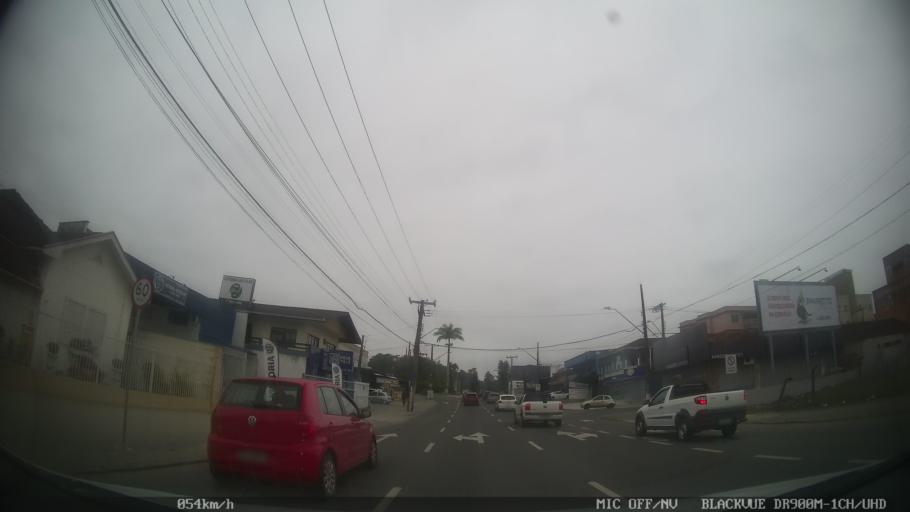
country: BR
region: Santa Catarina
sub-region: Joinville
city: Joinville
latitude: -26.3229
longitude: -48.8449
